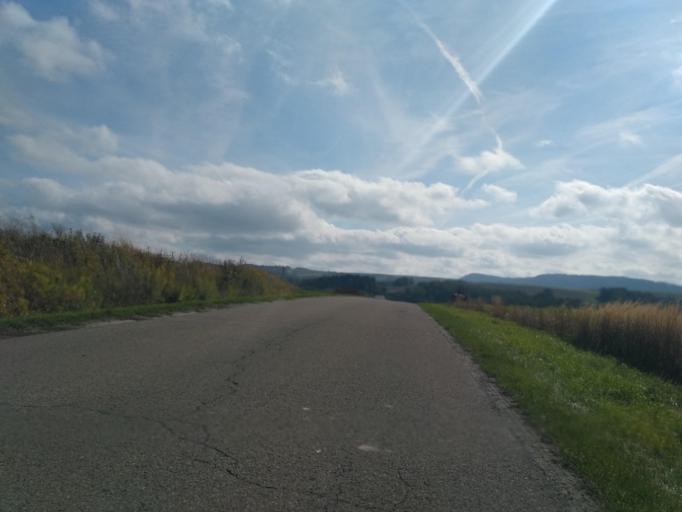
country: PL
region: Subcarpathian Voivodeship
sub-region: Powiat ropczycko-sedziszowski
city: Wielopole Skrzynskie
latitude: 49.9268
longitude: 21.5655
